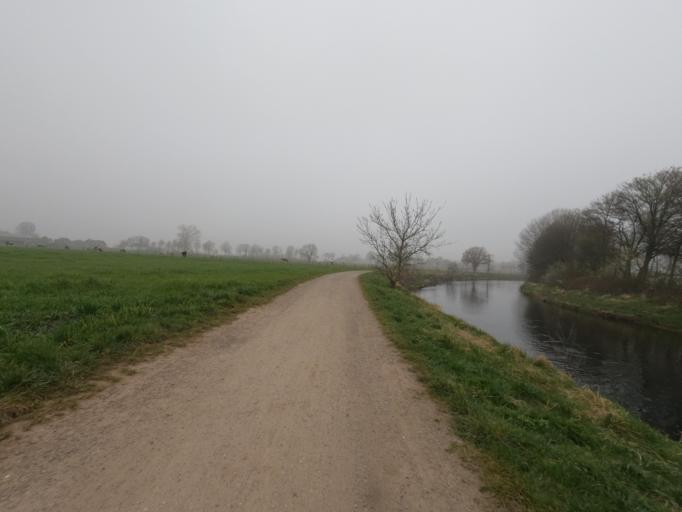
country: DE
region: North Rhine-Westphalia
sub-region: Regierungsbezirk Koln
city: Wassenberg
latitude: 51.0812
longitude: 6.1484
